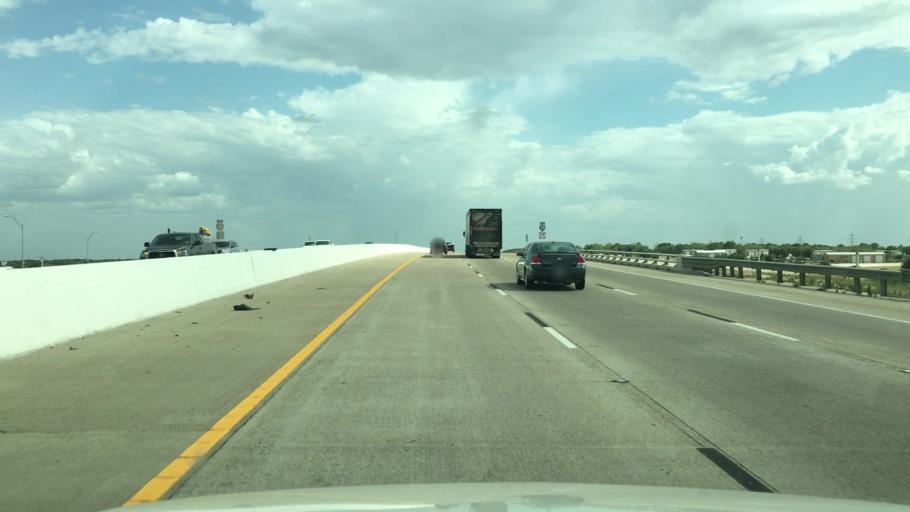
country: US
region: Texas
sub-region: McLennan County
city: Northcrest
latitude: 31.6900
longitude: -97.1001
